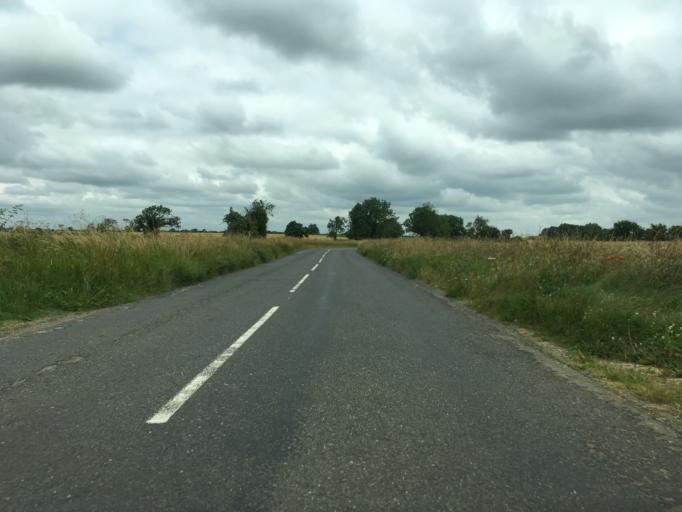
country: GB
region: England
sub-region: Oxfordshire
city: Charlbury
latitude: 51.9120
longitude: -1.4911
